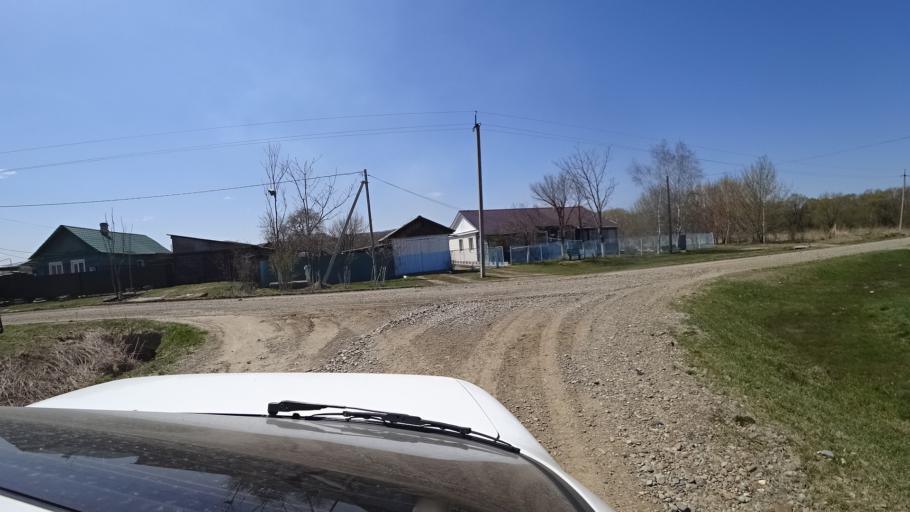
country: RU
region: Primorskiy
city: Lazo
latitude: 45.7934
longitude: 133.7639
